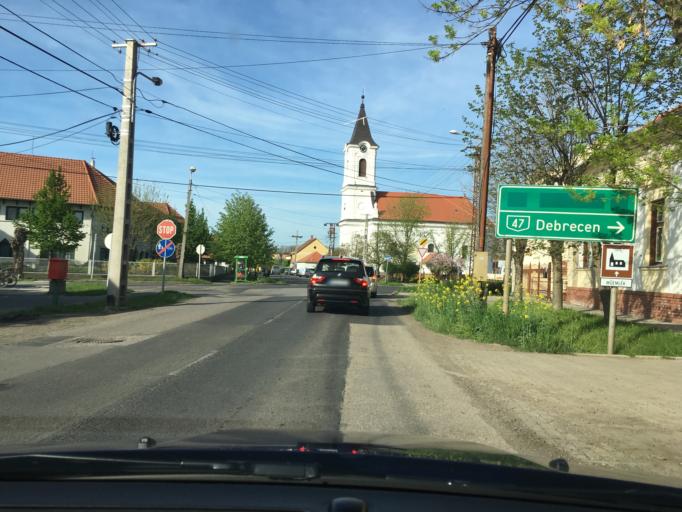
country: HU
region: Bekes
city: Mezobereny
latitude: 46.8170
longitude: 21.0223
